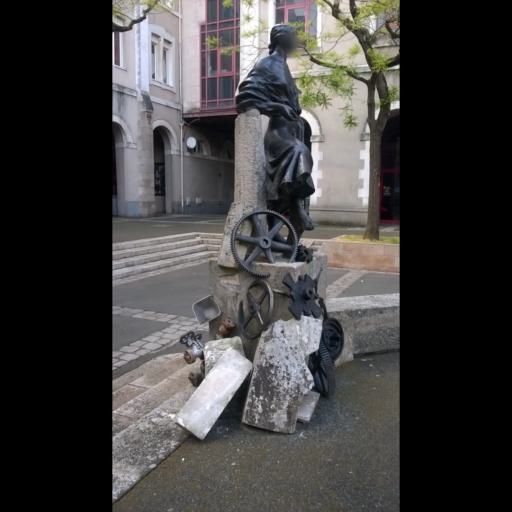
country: FR
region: Pays de la Loire
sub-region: Departement de la Loire-Atlantique
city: Nantes
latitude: 47.2201
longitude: -1.5355
